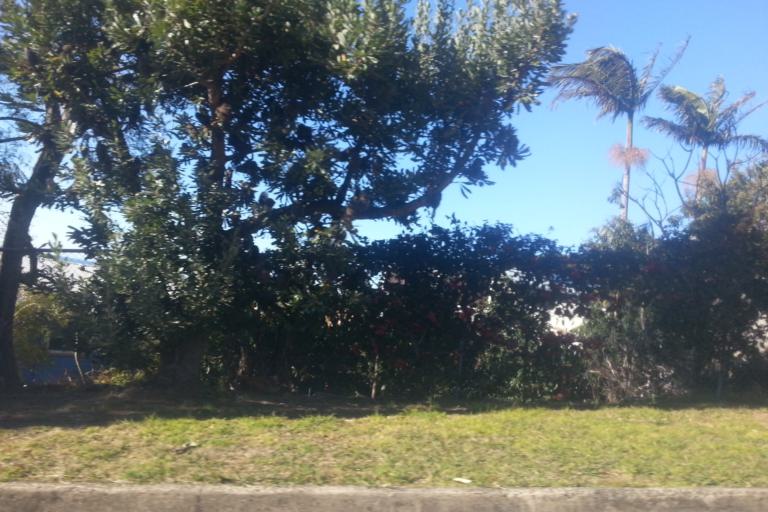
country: AU
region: New South Wales
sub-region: Wollongong
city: Bulli
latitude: -34.3146
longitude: 150.9077
